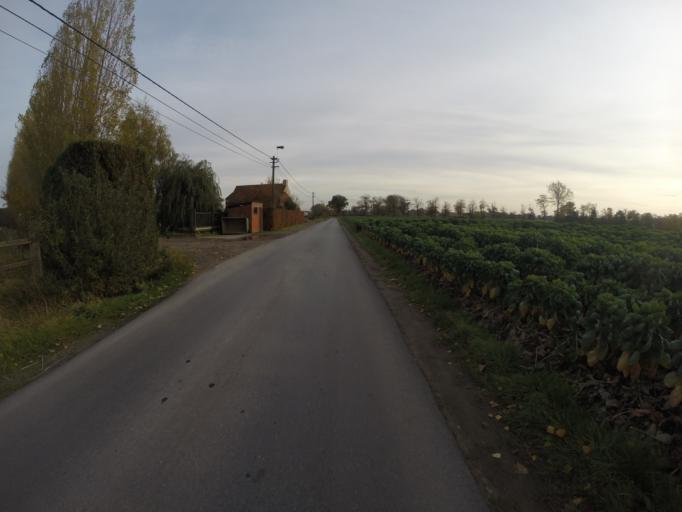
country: BE
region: Flanders
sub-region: Provincie Oost-Vlaanderen
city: Aalter
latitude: 51.0621
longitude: 3.4725
